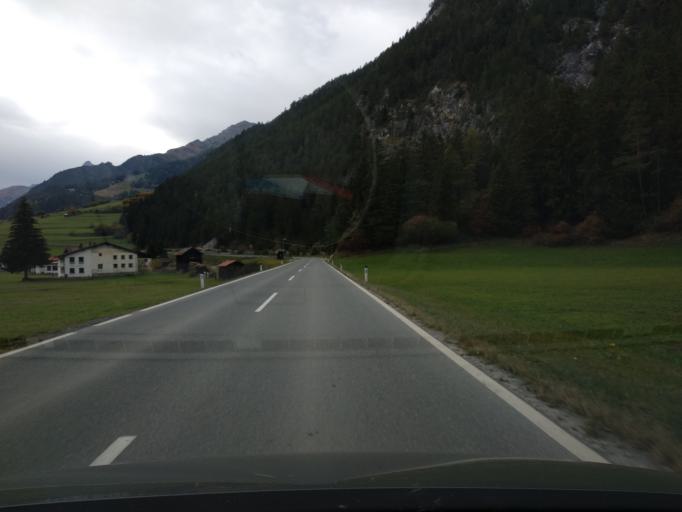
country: AT
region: Tyrol
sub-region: Politischer Bezirk Landeck
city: Flirsch
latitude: 47.1514
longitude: 10.3613
